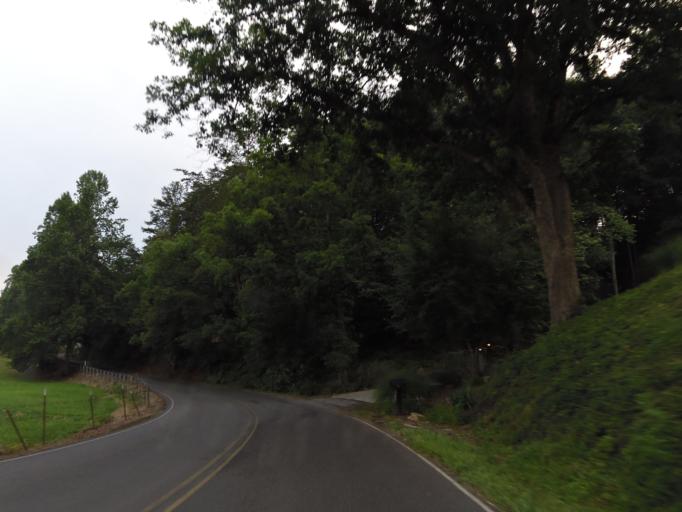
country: US
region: Tennessee
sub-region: Sevier County
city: Pigeon Forge
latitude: 35.7740
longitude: -83.6545
